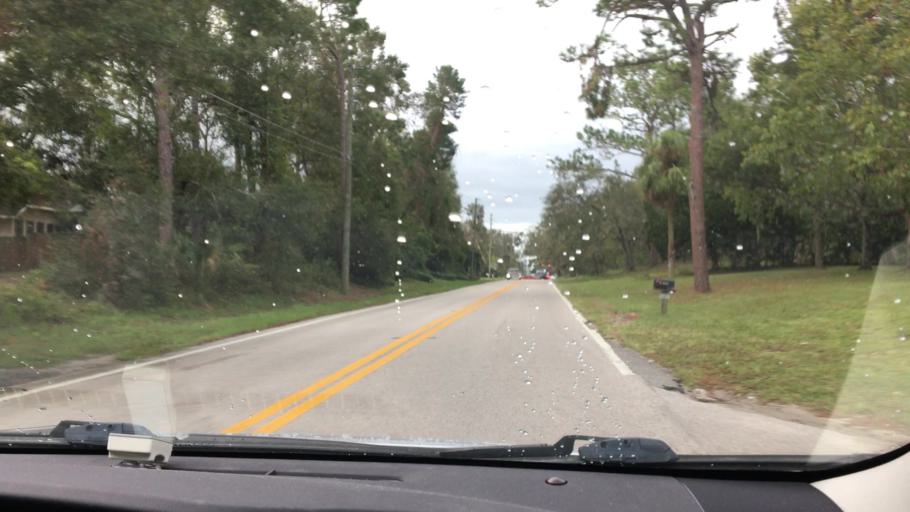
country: US
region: Florida
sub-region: Seminole County
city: Heathrow
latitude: 28.8158
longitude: -81.3631
